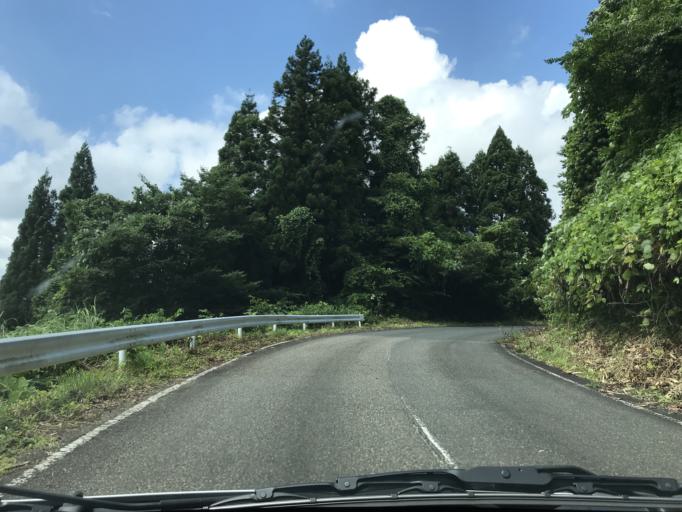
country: JP
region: Iwate
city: Mizusawa
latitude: 39.0610
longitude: 141.4023
